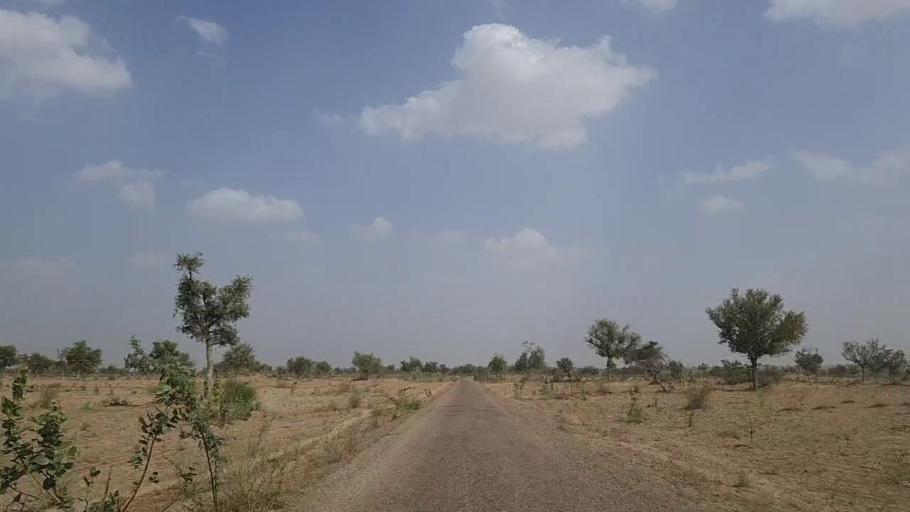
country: PK
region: Sindh
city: Islamkot
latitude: 24.8297
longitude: 70.1635
